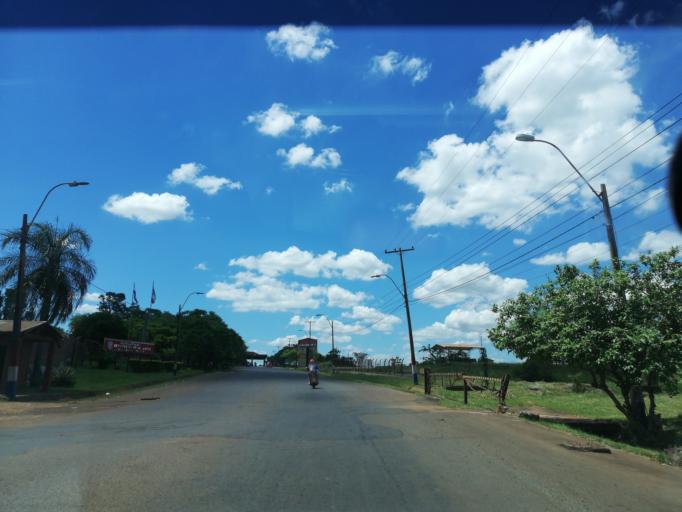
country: PY
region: Itapua
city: Encarnacion
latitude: -27.3662
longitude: -55.8547
